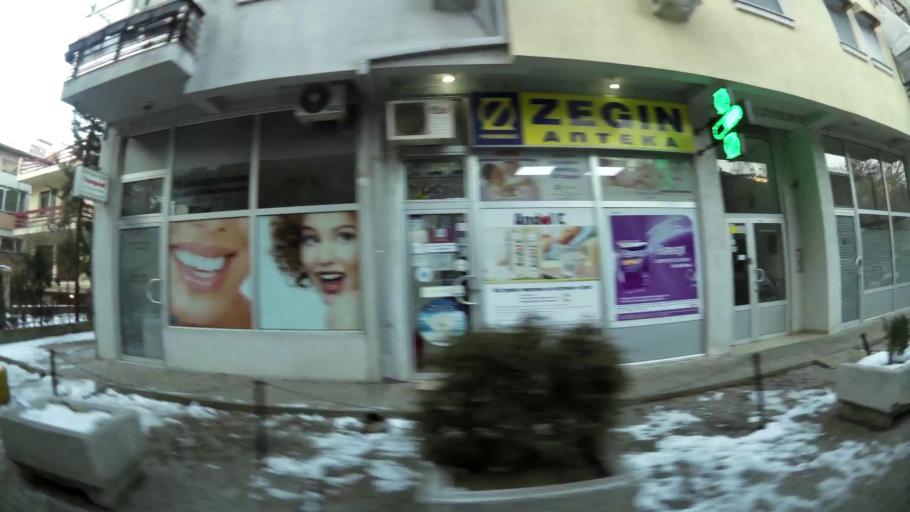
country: MK
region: Karpos
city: Skopje
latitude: 42.0026
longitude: 21.4115
